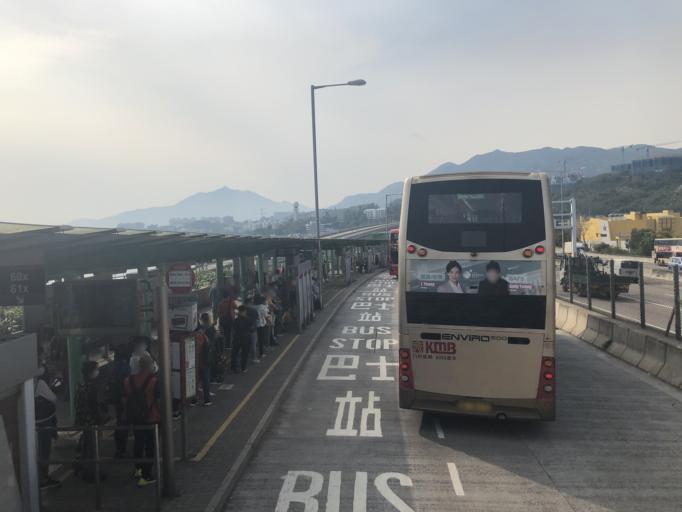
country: HK
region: Tuen Mun
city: Tuen Mun
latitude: 22.3578
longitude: 114.0195
